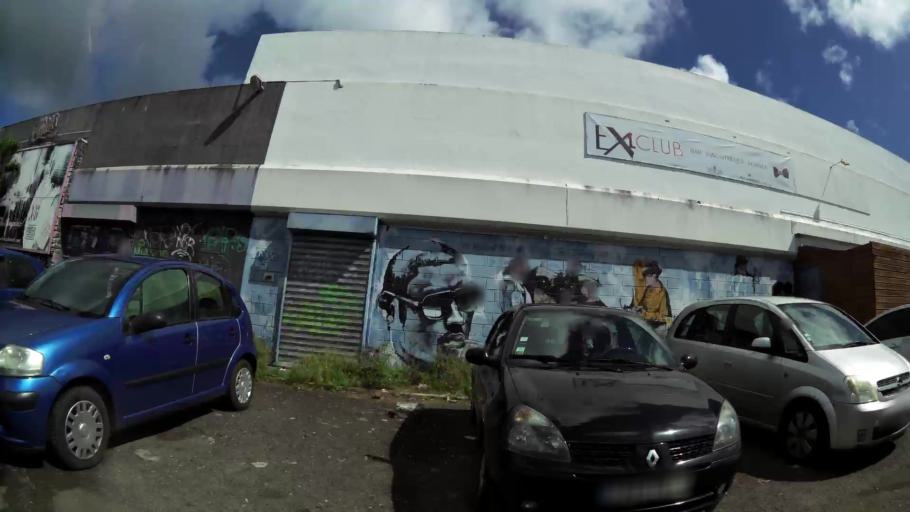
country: GP
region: Guadeloupe
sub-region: Guadeloupe
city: Pointe-a-Pitre
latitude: 16.2551
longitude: -61.5247
